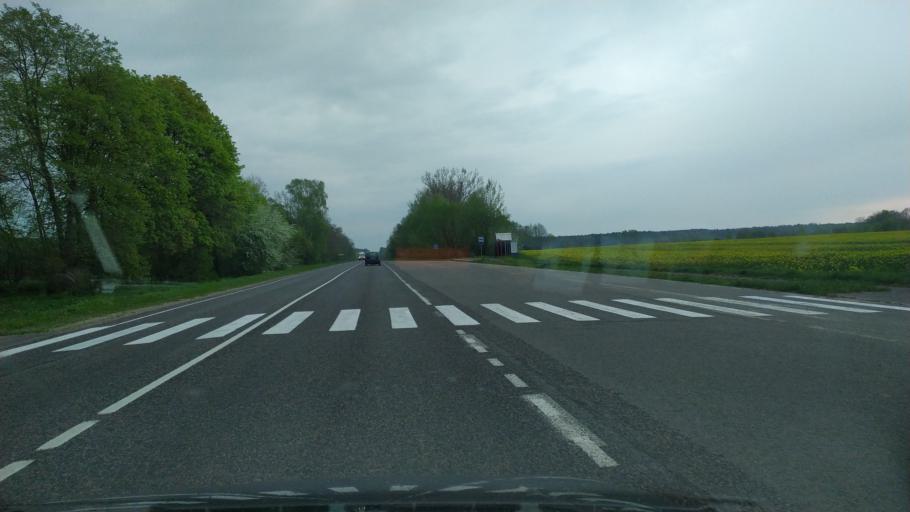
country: BY
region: Brest
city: Horad Kobryn
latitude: 52.2915
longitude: 24.5021
